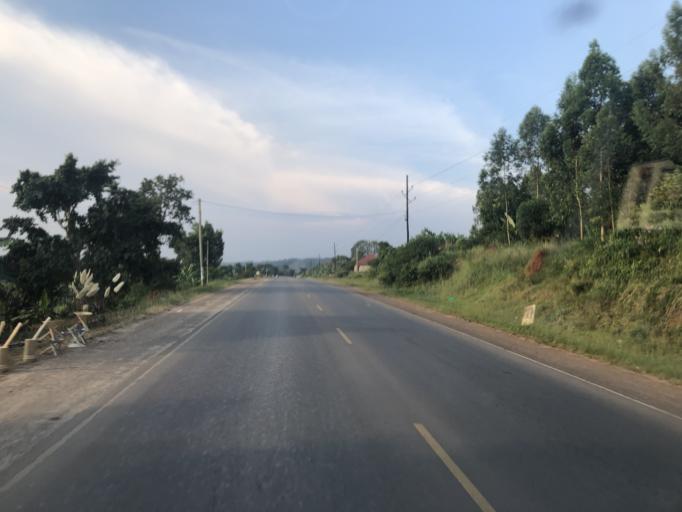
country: UG
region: Central Region
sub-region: Mpigi District
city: Mpigi
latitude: 0.1968
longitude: 32.2979
